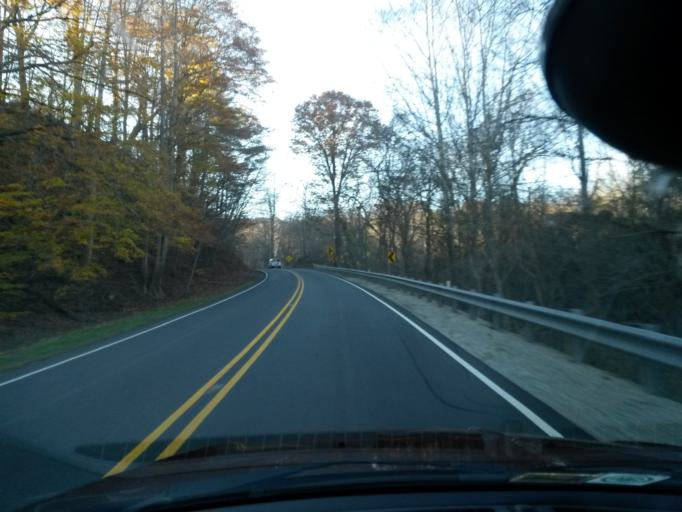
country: US
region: Virginia
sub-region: City of Buena Vista
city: Buena Vista
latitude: 37.6860
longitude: -79.2297
